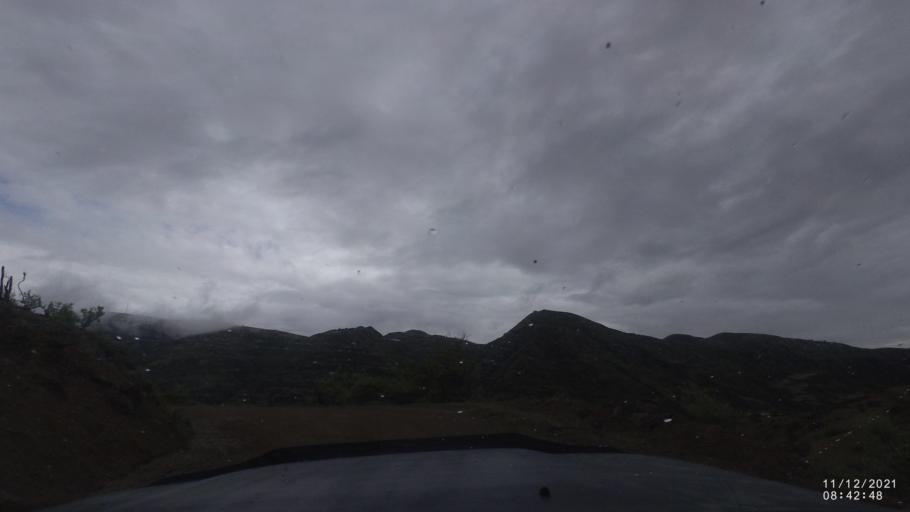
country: BO
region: Cochabamba
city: Tarata
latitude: -17.9152
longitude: -65.9358
